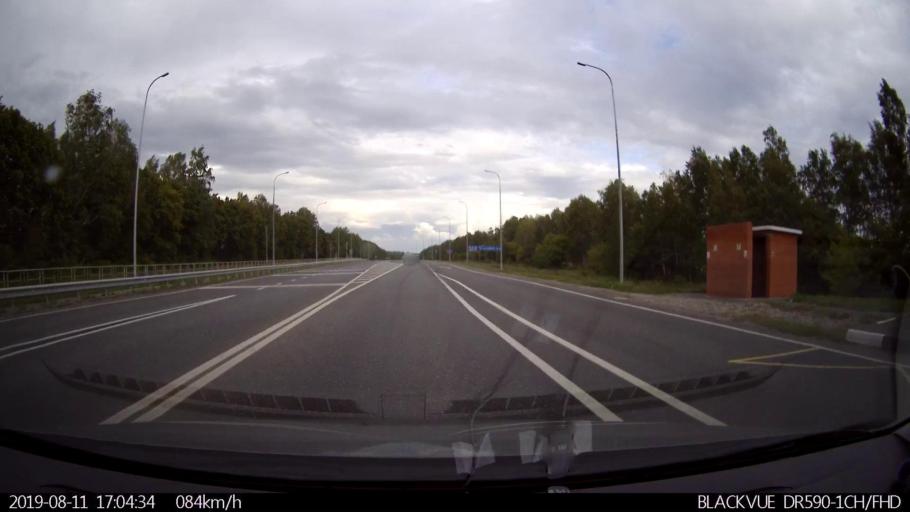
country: RU
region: Ulyanovsk
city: Mayna
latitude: 54.3004
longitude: 47.7666
